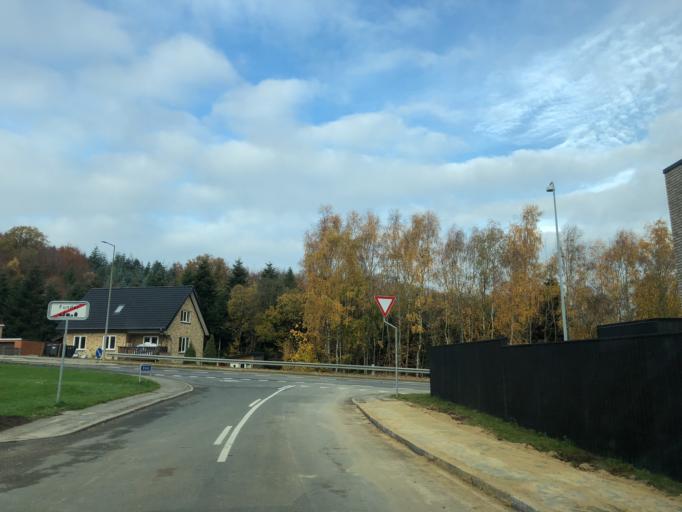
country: DK
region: Central Jutland
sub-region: Silkeborg Kommune
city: Silkeborg
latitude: 56.1510
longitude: 9.4900
